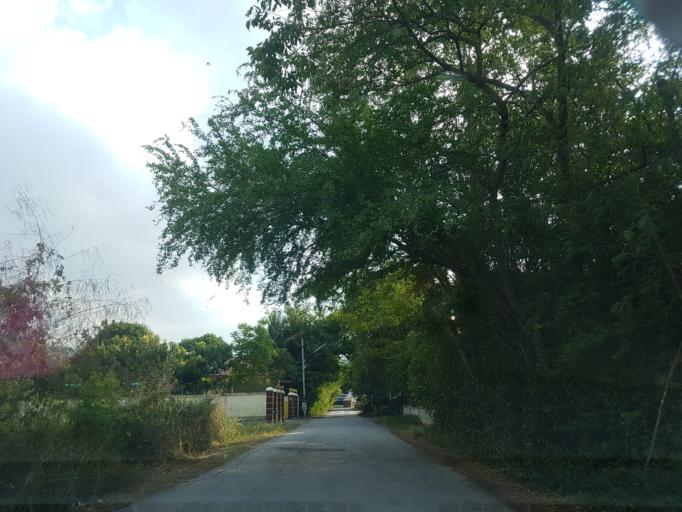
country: TH
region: Lop Buri
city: Lop Buri
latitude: 14.7715
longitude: 100.6969
